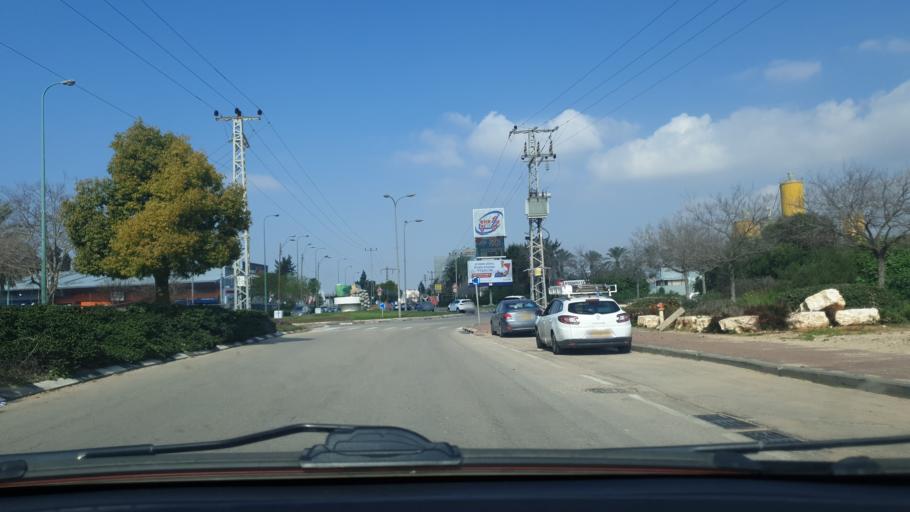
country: IL
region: Tel Aviv
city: Azor
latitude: 32.0072
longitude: 34.8077
